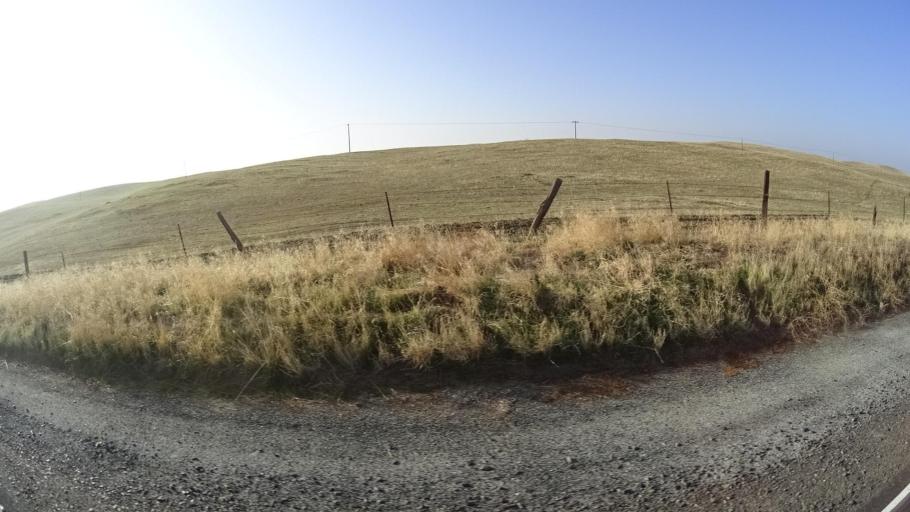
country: US
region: California
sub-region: Tulare County
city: Richgrove
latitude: 35.7497
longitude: -118.9935
